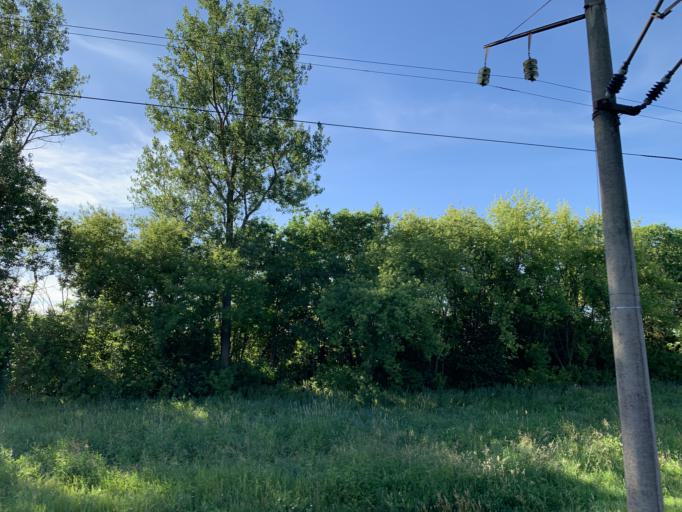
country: BY
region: Minsk
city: Novy Svyerzhan'
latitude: 53.4048
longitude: 26.6303
